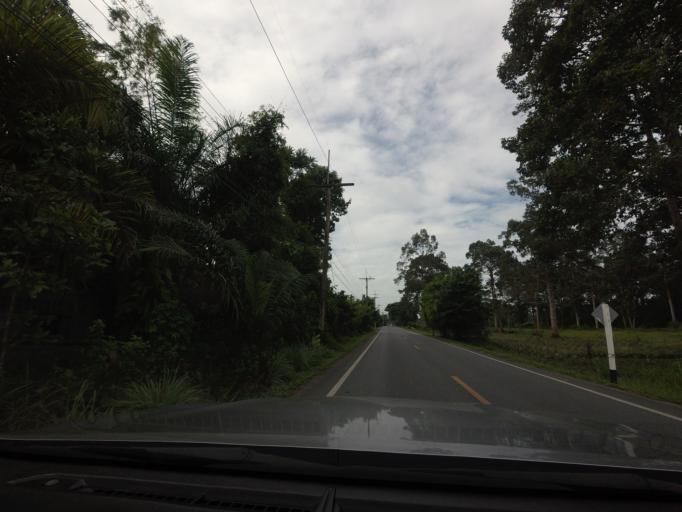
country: TH
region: Nakhon Si Thammarat
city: Phra Phrom
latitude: 8.2771
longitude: 99.9441
